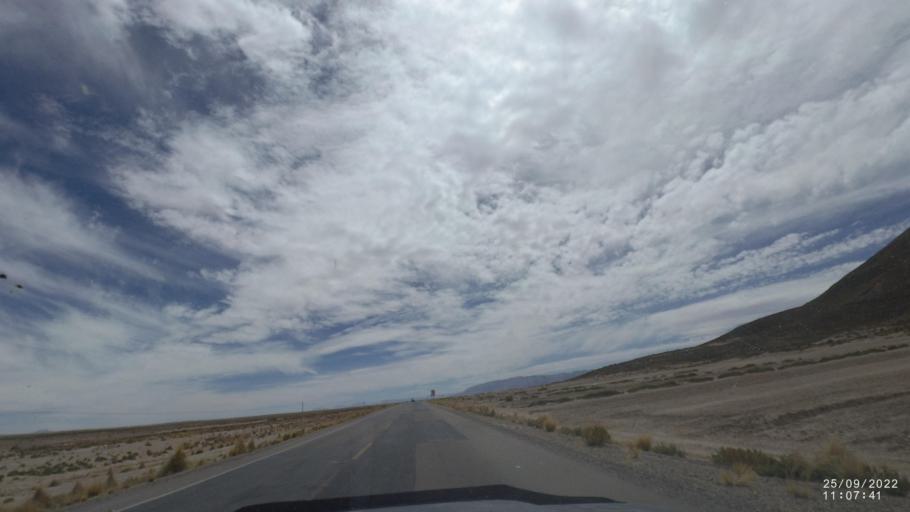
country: BO
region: Oruro
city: Challapata
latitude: -19.3398
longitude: -66.8541
